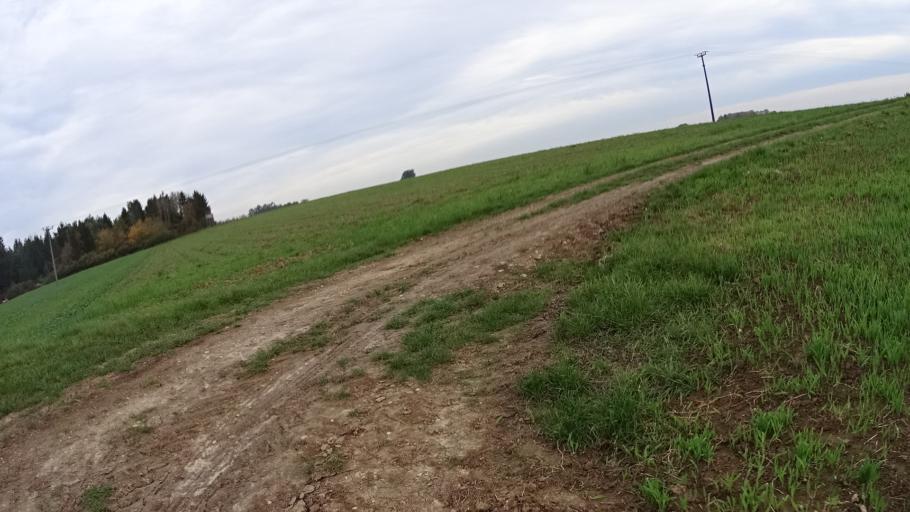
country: DE
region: Bavaria
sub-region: Upper Bavaria
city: Hitzhofen
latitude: 48.8389
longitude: 11.3026
